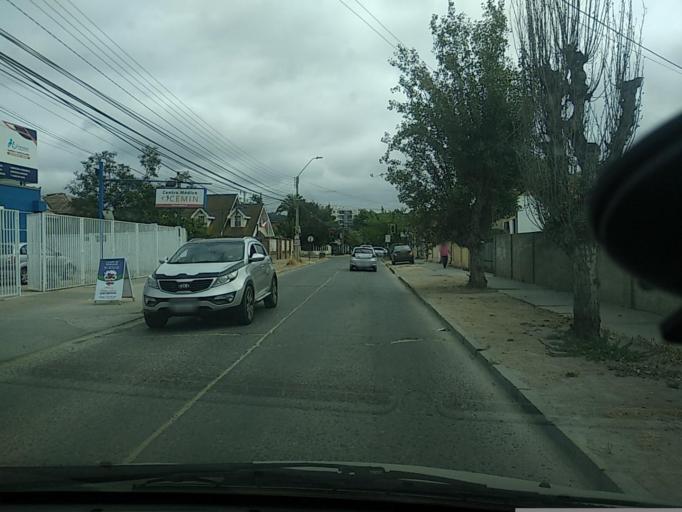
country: CL
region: Valparaiso
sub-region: Provincia de Marga Marga
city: Villa Alemana
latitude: -33.0401
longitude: -71.3759
